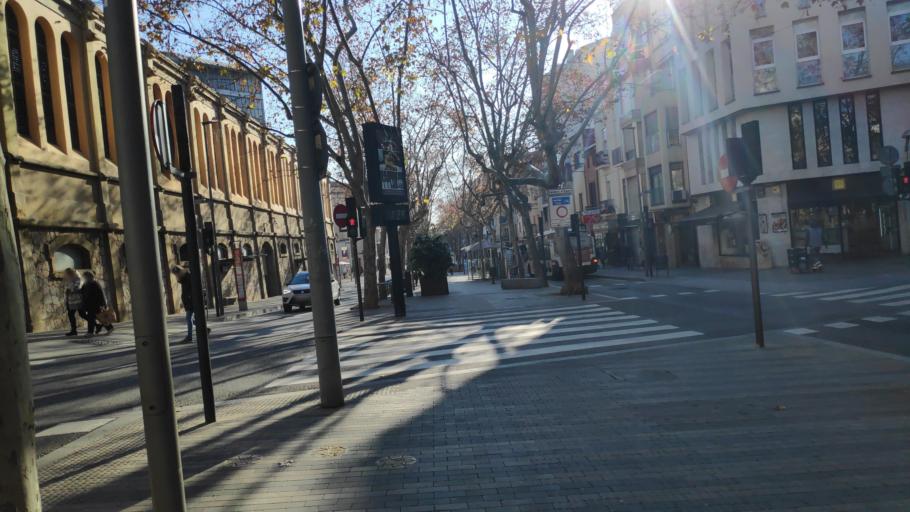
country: ES
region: Catalonia
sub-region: Provincia de Barcelona
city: Terrassa
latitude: 41.5638
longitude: 2.0078
